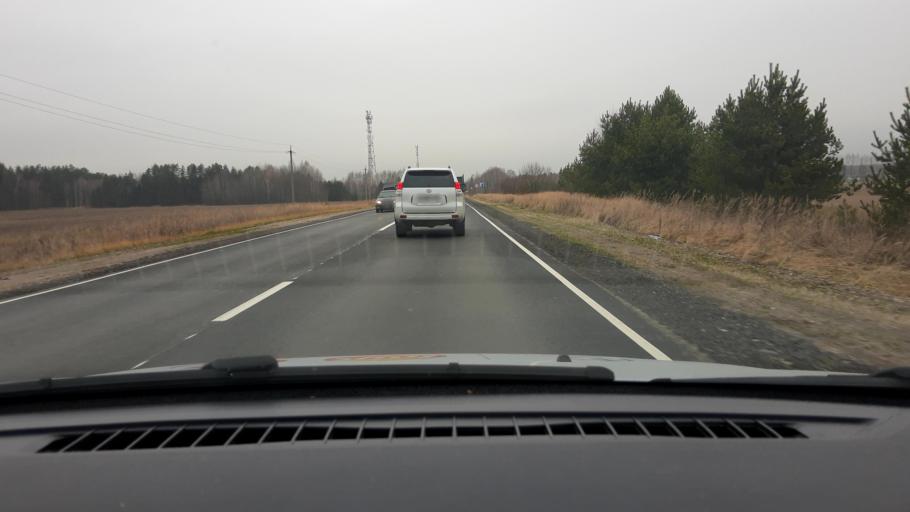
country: RU
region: Nizjnij Novgorod
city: Novaya Balakhna
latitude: 56.5947
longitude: 43.6501
